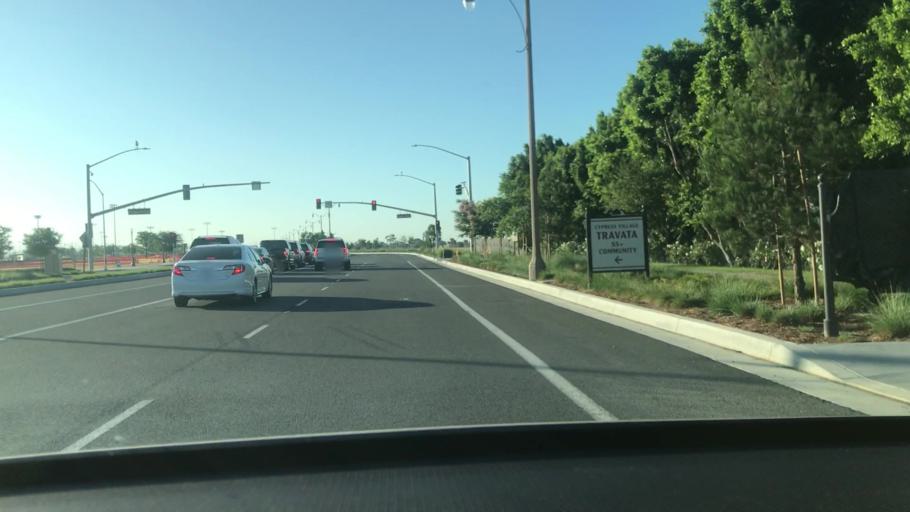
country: US
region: California
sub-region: Orange County
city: Lake Forest
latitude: 33.6736
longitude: -117.7519
